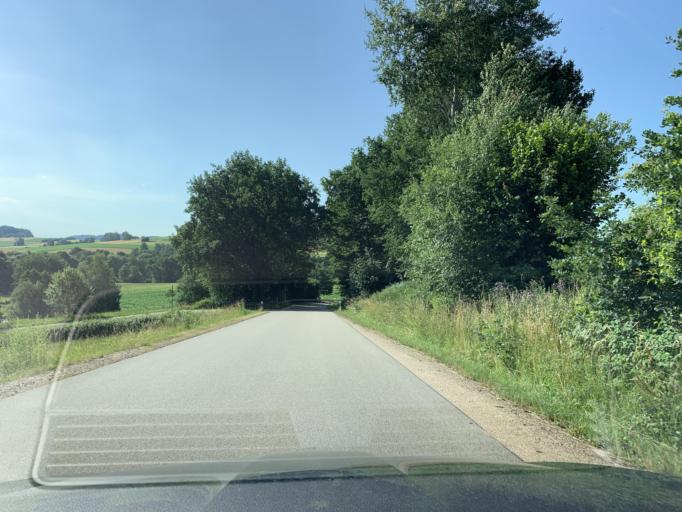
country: DE
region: Bavaria
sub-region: Upper Palatinate
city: Dieterskirchen
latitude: 49.4078
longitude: 12.4152
